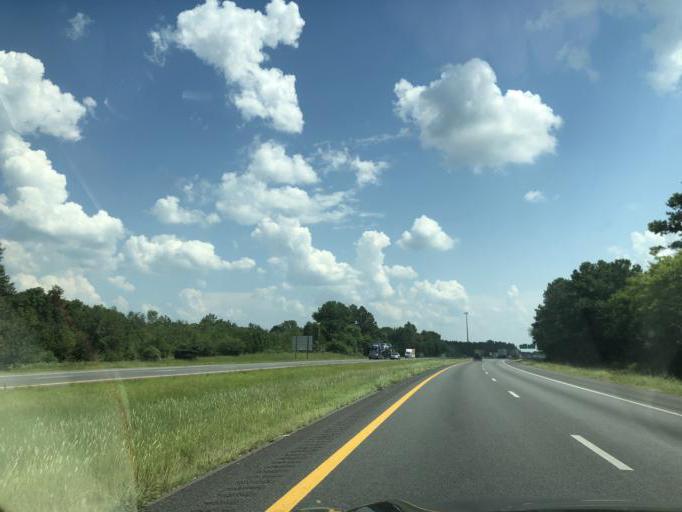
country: US
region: Tennessee
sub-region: Rutherford County
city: Murfreesboro
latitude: 35.7973
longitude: -86.3806
